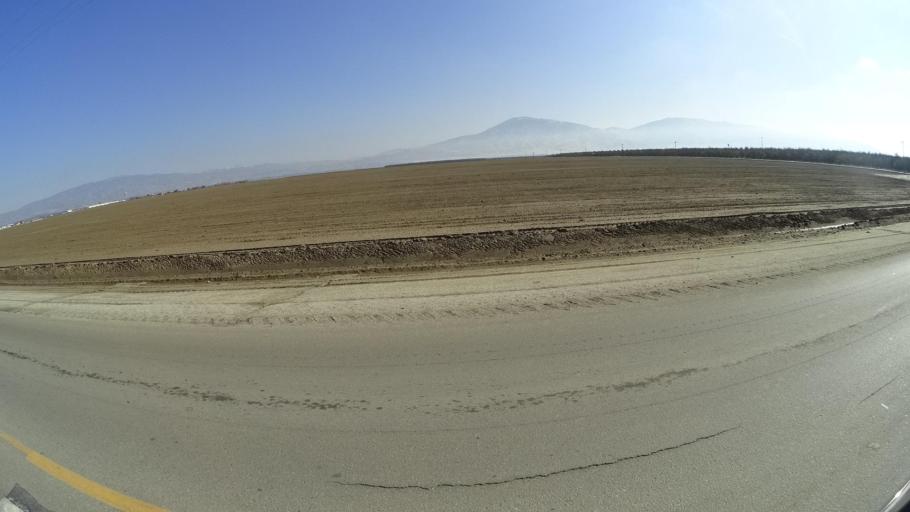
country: US
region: California
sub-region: Kern County
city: Arvin
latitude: 35.2397
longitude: -118.8605
